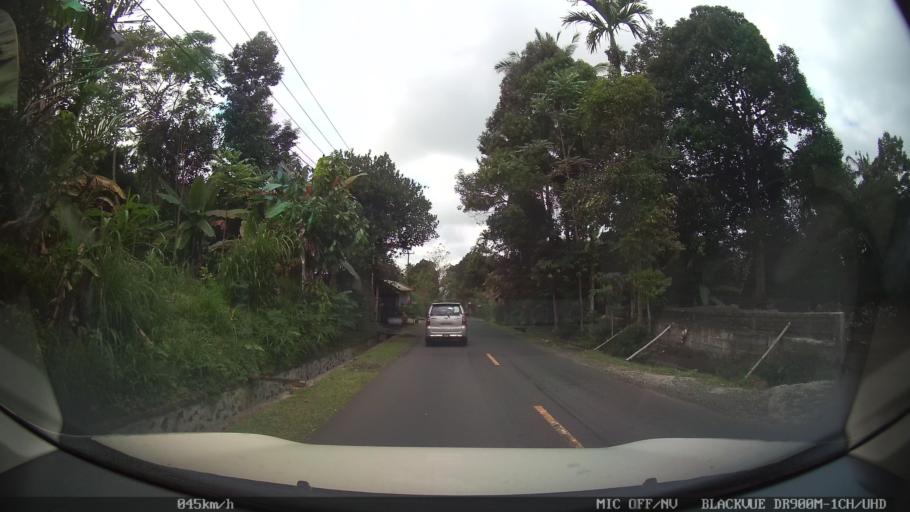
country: ID
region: Bali
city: Banjar Geriana Kangin
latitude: -8.3979
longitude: 115.4337
